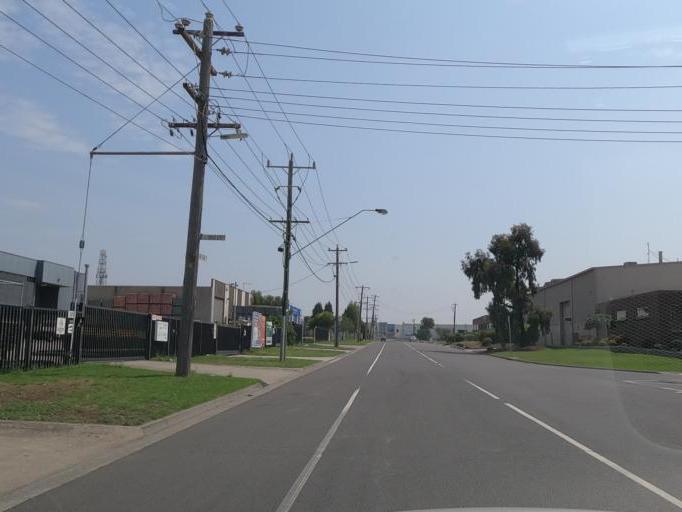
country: AU
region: Victoria
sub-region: Hume
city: Coolaroo
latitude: -37.6478
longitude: 144.9465
